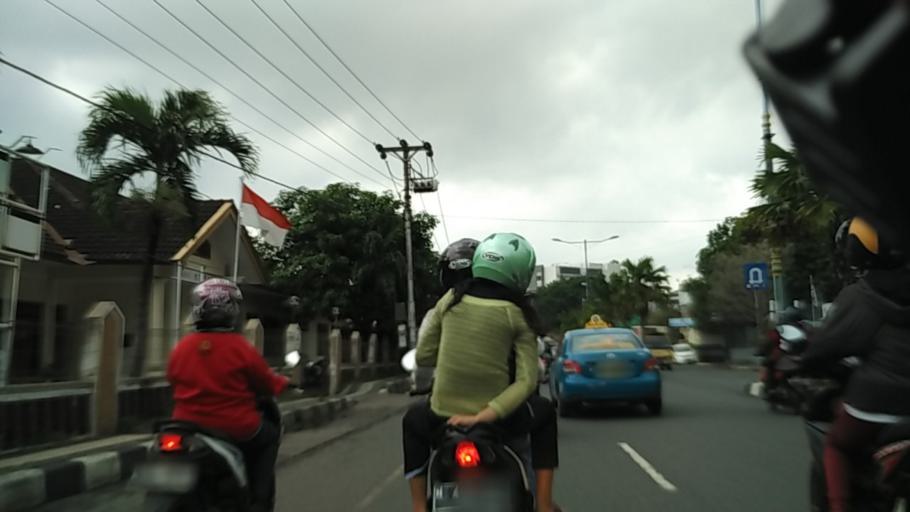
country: ID
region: Central Java
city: Semarang
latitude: -6.9955
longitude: 110.4055
